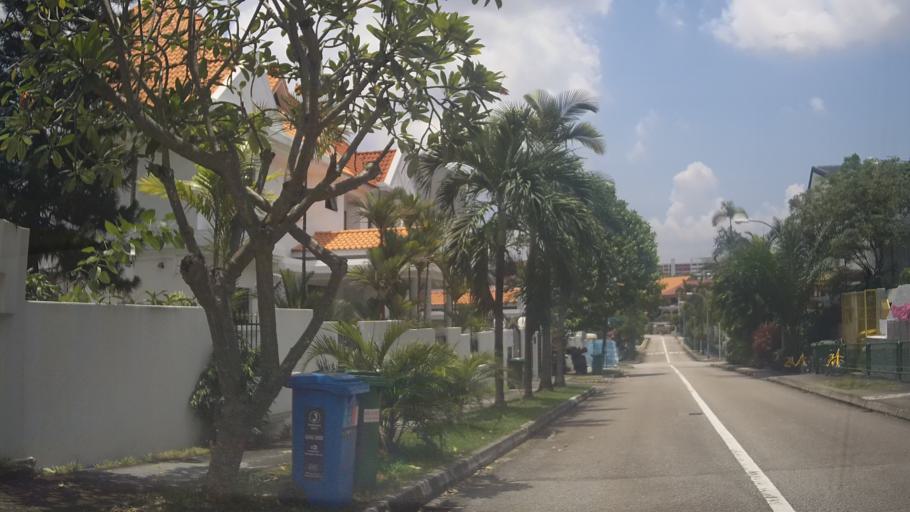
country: SG
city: Singapore
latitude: 1.3603
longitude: 103.8728
